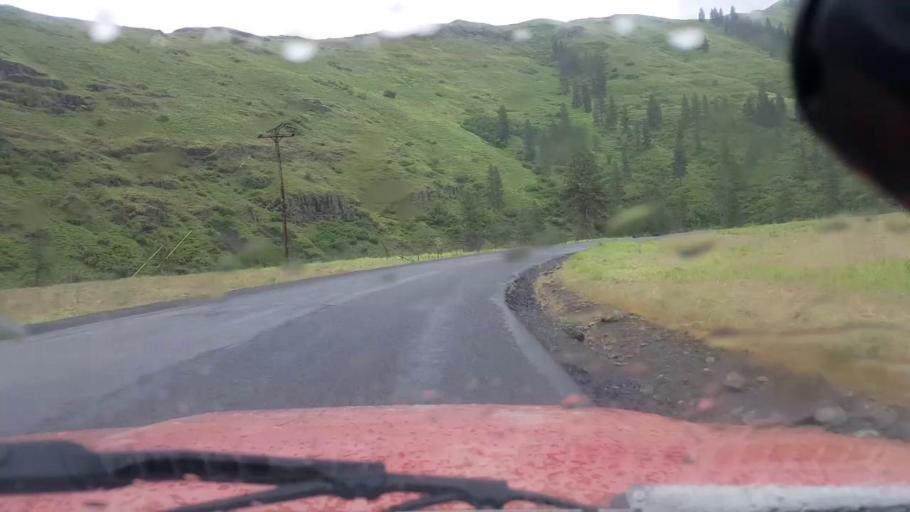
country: US
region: Washington
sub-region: Asotin County
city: Asotin
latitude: 46.0286
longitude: -117.3246
